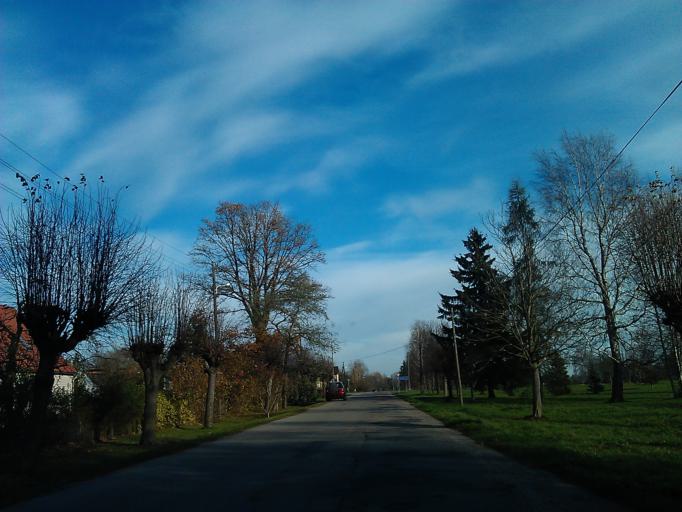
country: LV
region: Aizpute
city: Aizpute
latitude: 56.7219
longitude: 21.6107
